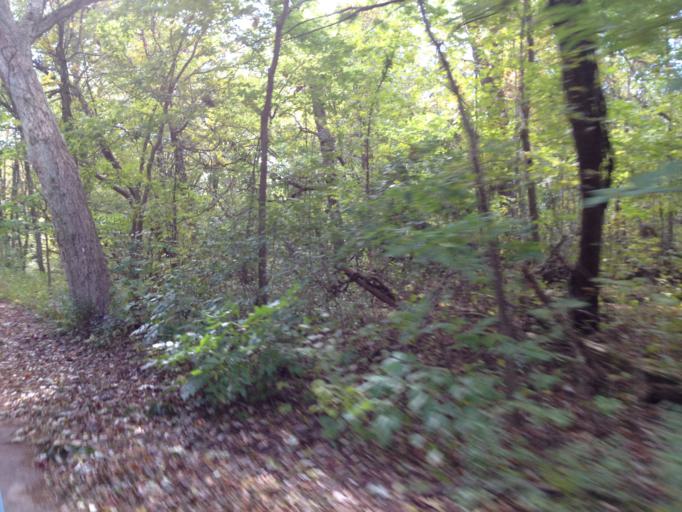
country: US
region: Ohio
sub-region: Erie County
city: Sandusky
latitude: 41.9302
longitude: -82.5140
